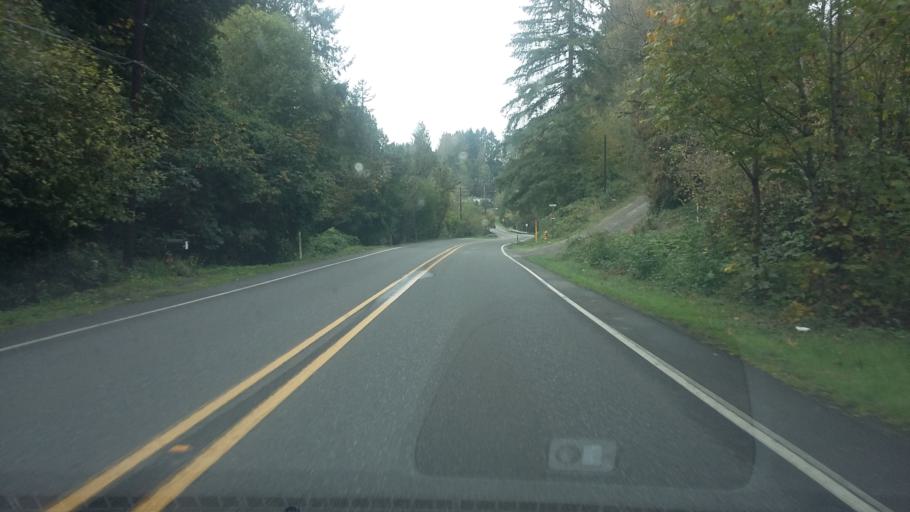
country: US
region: Washington
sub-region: Clark County
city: Ridgefield
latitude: 45.8156
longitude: -122.7277
